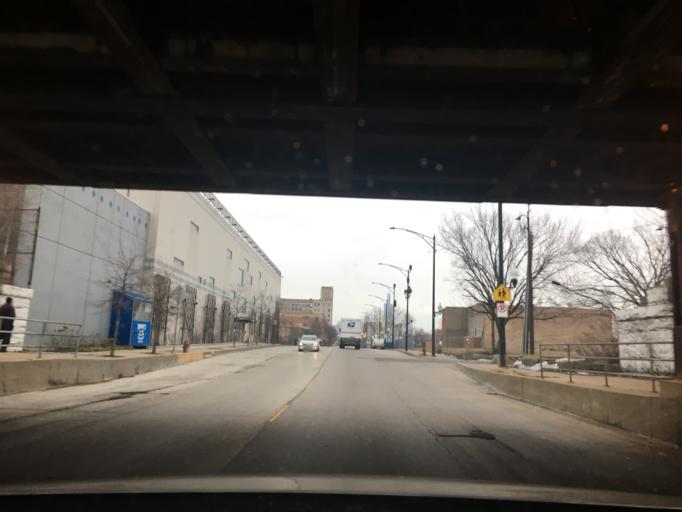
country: US
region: Illinois
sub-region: Cook County
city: Chicago
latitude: 41.8811
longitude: -87.6918
